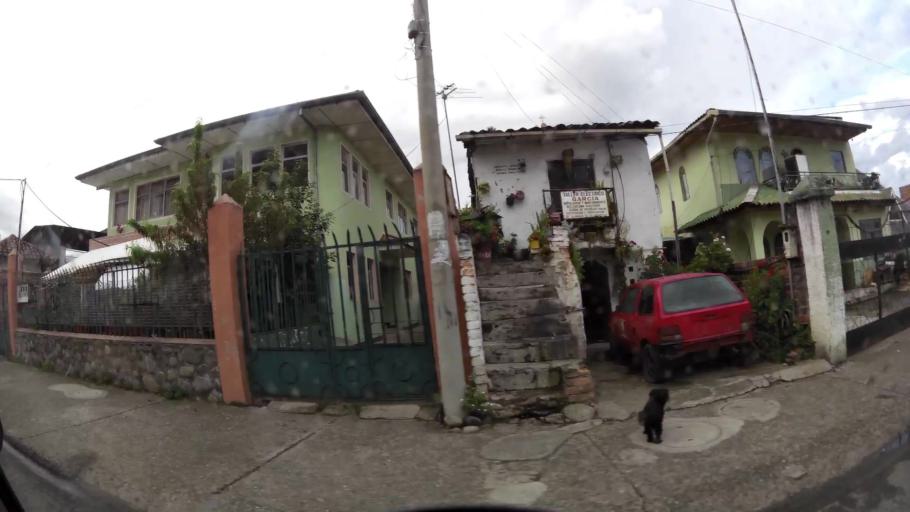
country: EC
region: Azuay
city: Cuenca
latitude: -2.8965
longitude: -79.0212
